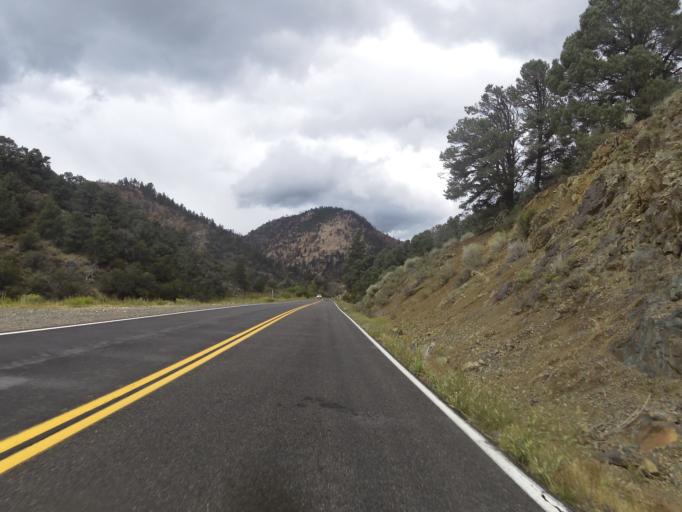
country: US
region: Nevada
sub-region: Douglas County
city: Gardnerville Ranchos
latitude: 38.6596
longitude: -119.6817
